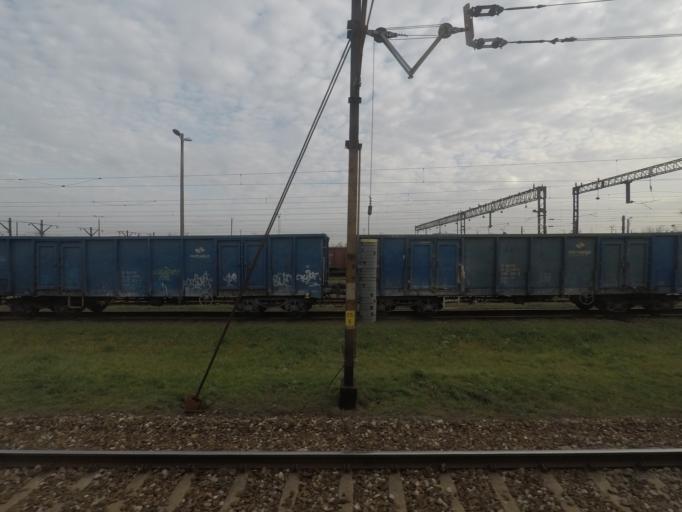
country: PL
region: Subcarpathian Voivodeship
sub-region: Powiat przemyski
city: Orly
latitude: 49.8379
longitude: 22.8415
